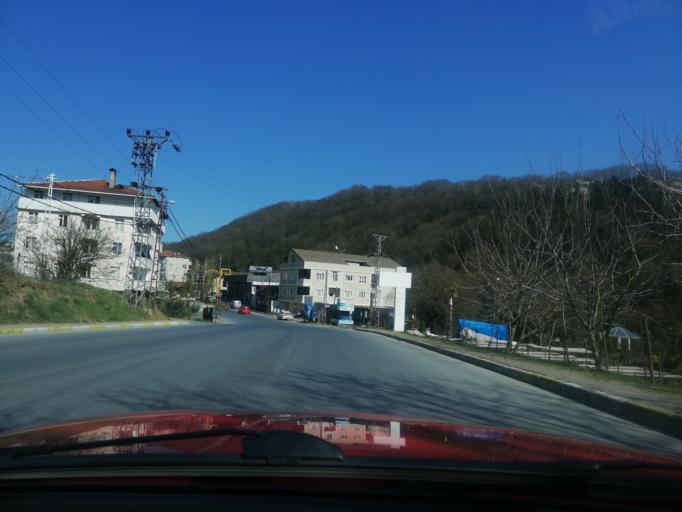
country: TR
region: Istanbul
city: Mahmut Sevket Pasa
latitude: 41.0948
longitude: 29.1452
